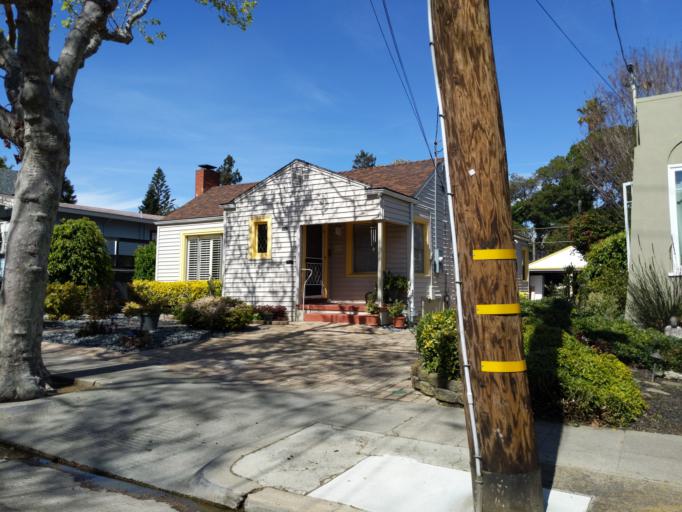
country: US
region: California
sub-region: Alameda County
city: Alameda
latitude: 37.7574
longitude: -122.2308
